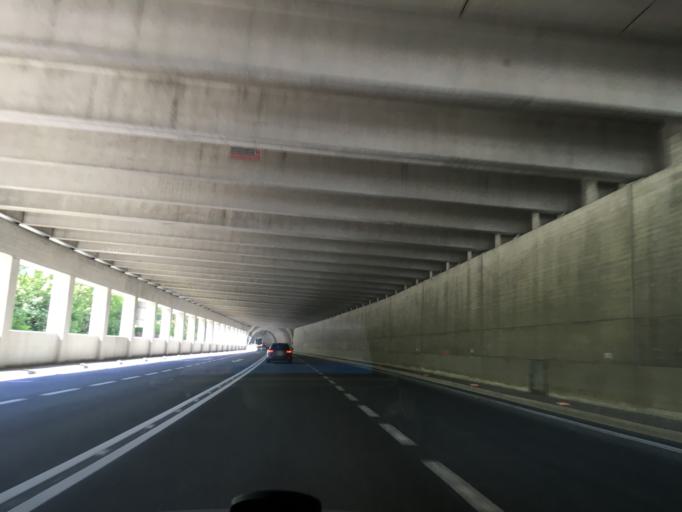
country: AT
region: Tyrol
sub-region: Politischer Bezirk Landeck
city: Zams
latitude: 47.1674
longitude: 10.5871
